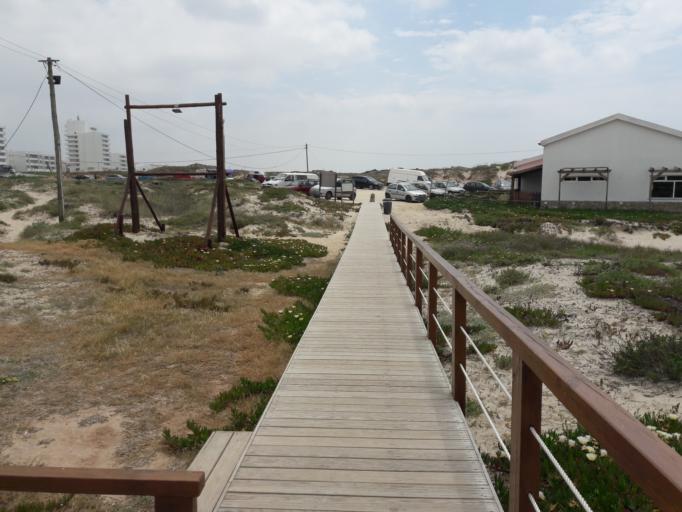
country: PT
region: Leiria
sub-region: Peniche
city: Atouguia da Baleia
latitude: 39.3675
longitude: -9.3387
